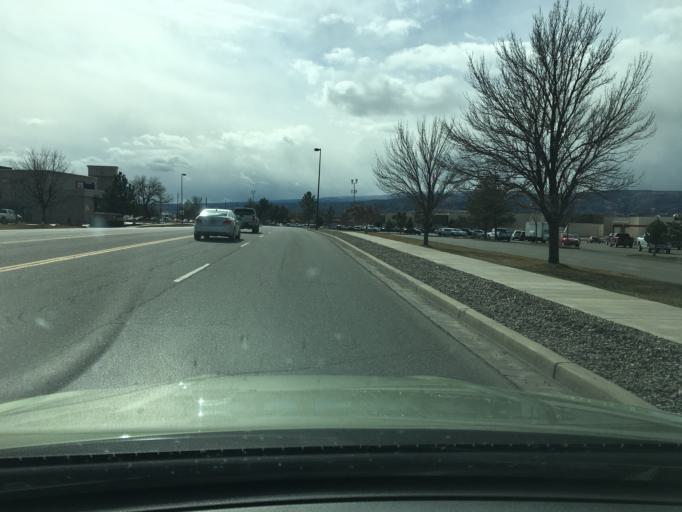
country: US
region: Colorado
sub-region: Mesa County
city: Redlands
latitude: 39.0935
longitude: -108.5998
